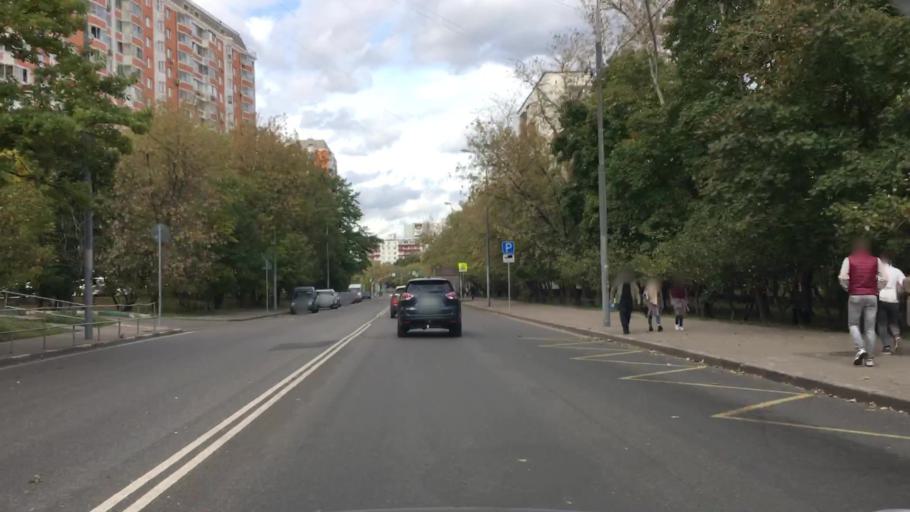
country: RU
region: Moscow
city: Gol'yanovo
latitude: 55.8077
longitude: 37.8180
